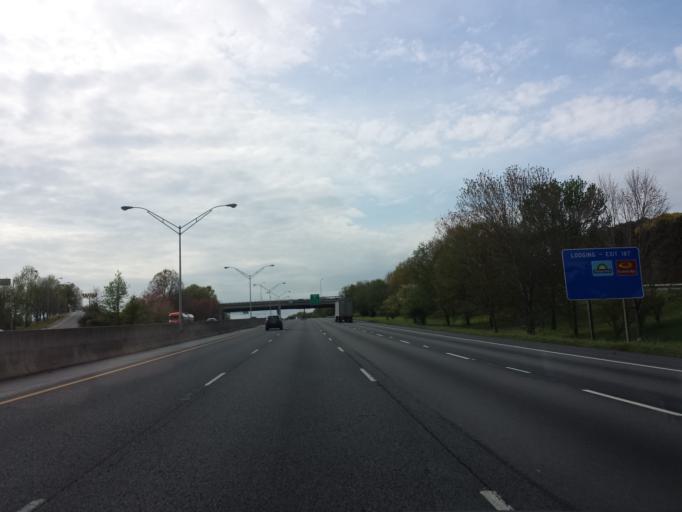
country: US
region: Georgia
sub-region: Monroe County
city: Forsyth
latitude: 33.0338
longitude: -83.9191
